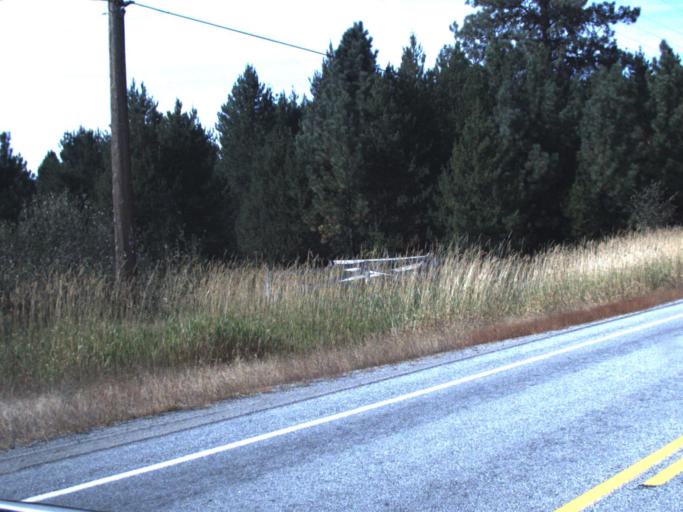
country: US
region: Washington
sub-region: Pend Oreille County
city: Newport
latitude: 48.2496
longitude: -117.2844
